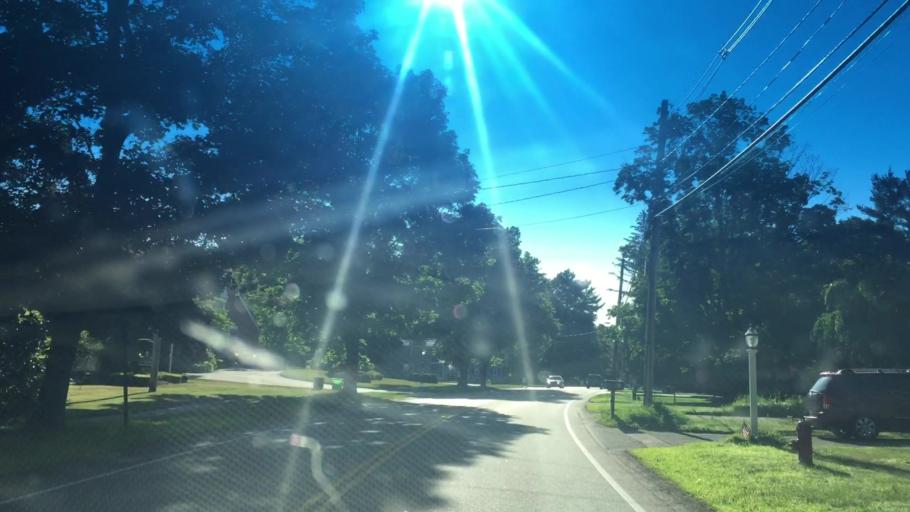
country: US
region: Massachusetts
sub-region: Norfolk County
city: Norfolk
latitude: 42.1208
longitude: -71.3170
